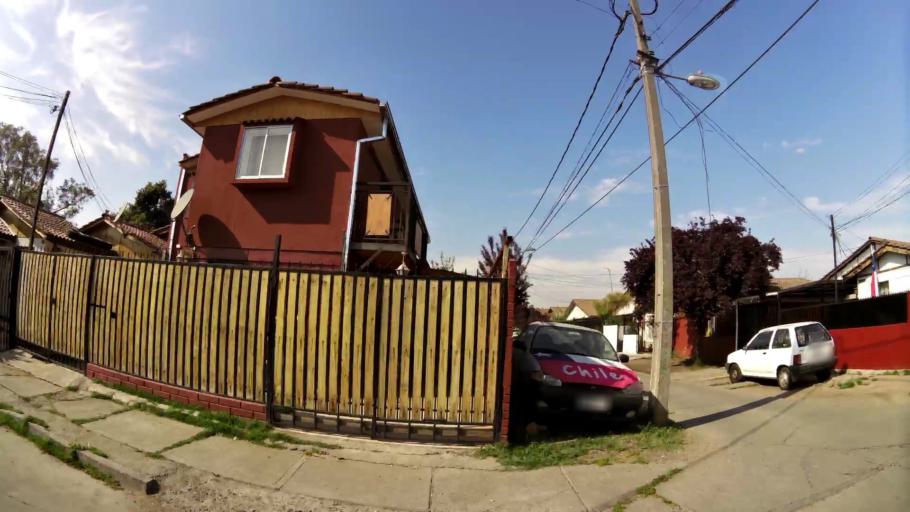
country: CL
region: Santiago Metropolitan
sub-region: Provincia de Santiago
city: La Pintana
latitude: -33.5568
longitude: -70.5936
